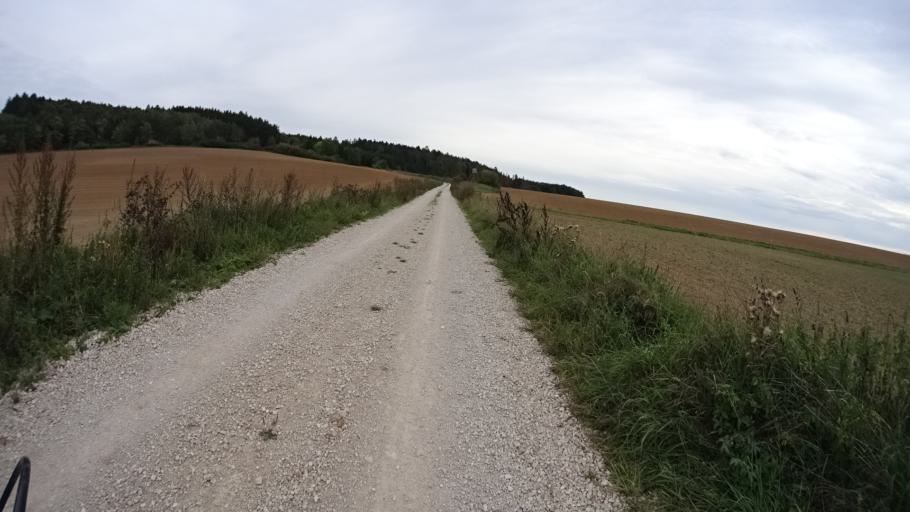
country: DE
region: Bavaria
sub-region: Upper Bavaria
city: Hitzhofen
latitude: 48.8530
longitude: 11.3396
